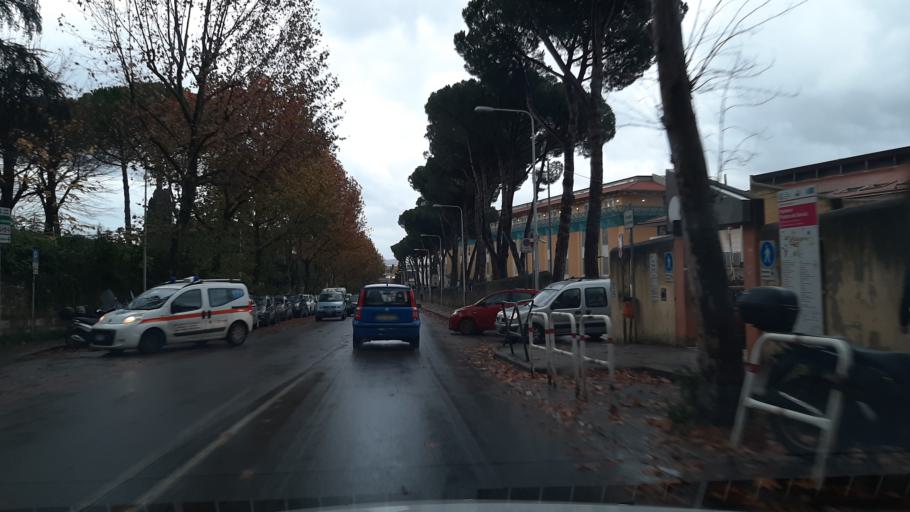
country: IT
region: Tuscany
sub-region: Province of Florence
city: Florence
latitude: 43.8069
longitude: 11.2498
